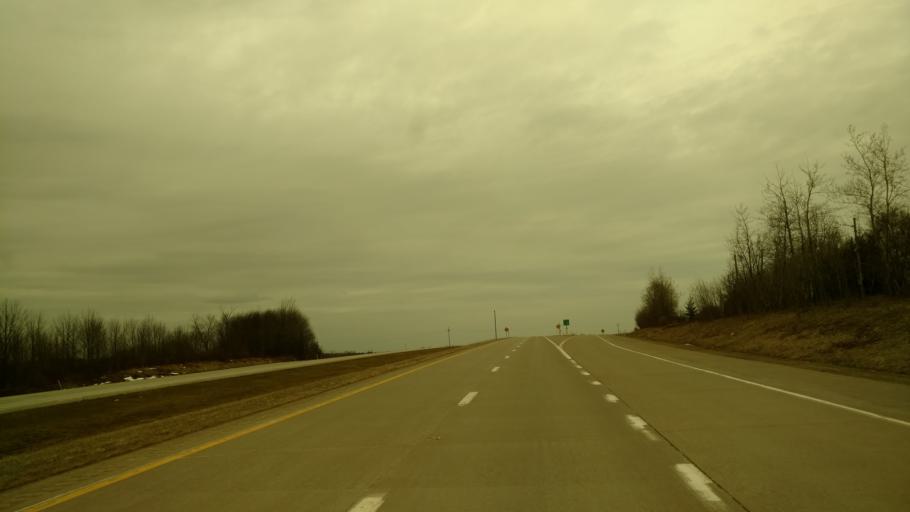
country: US
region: Pennsylvania
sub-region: Erie County
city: North East
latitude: 42.1355
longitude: -79.8173
